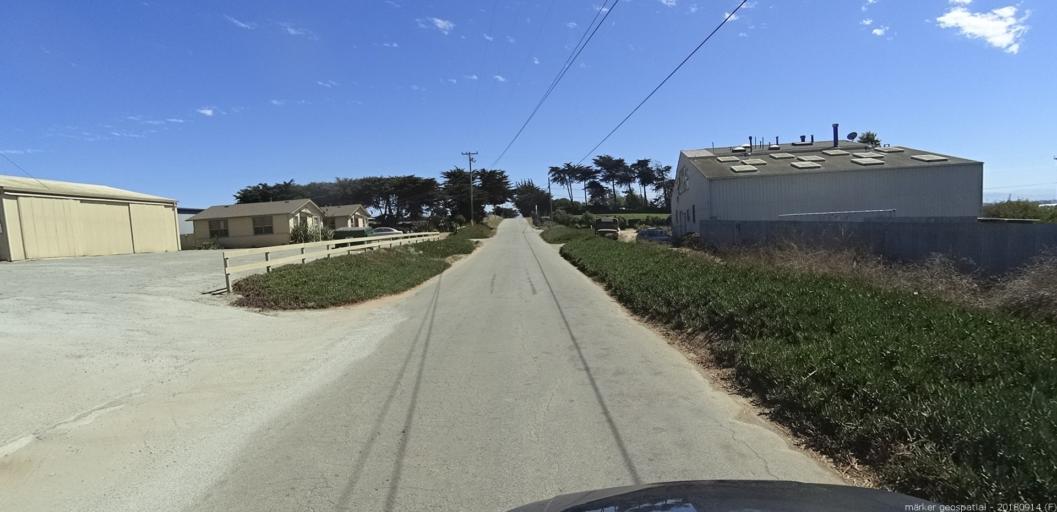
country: US
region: California
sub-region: Monterey County
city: Las Lomas
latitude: 36.8553
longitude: -121.7934
